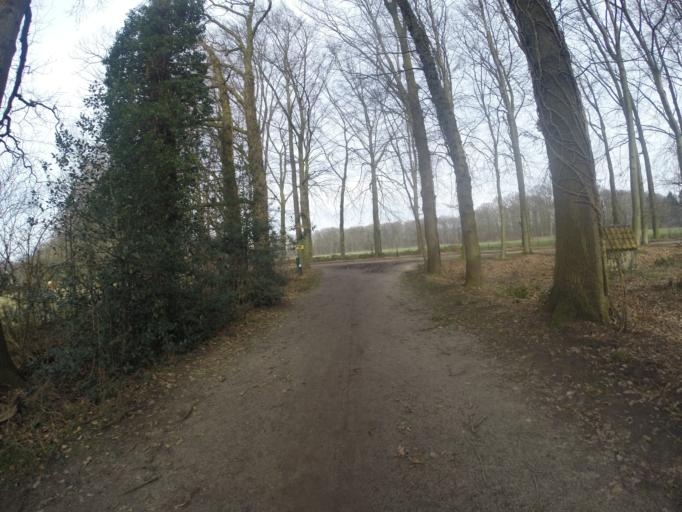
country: NL
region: Gelderland
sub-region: Gemeente Bronckhorst
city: Hengelo
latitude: 52.0981
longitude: 6.2859
